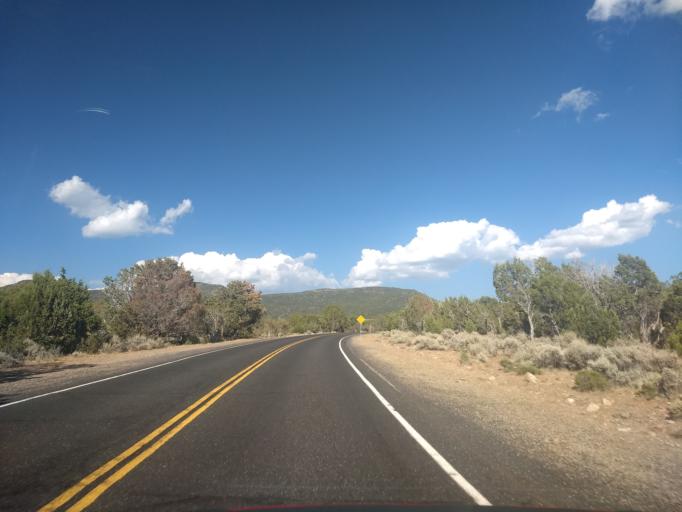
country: US
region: Utah
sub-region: Washington County
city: Enterprise
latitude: 37.4180
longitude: -113.5607
